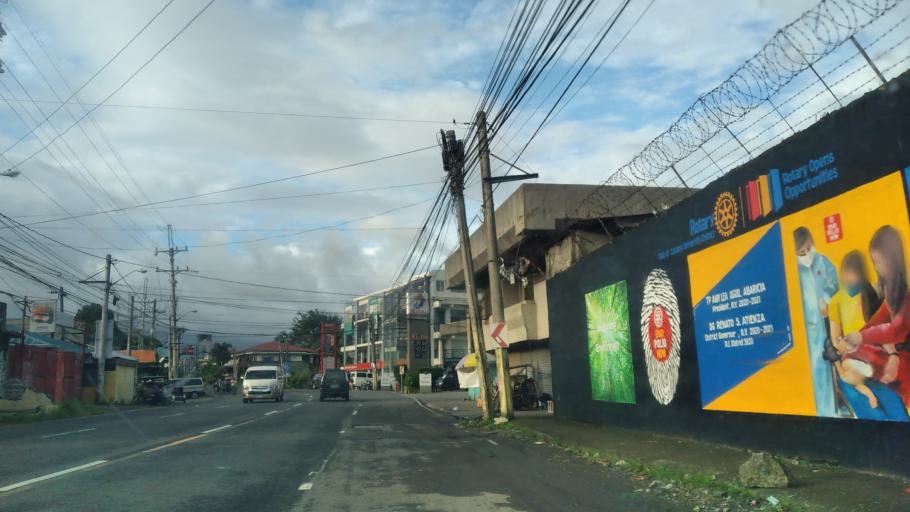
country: PH
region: Calabarzon
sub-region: Province of Quezon
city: Lucena
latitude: 13.9493
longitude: 121.6140
